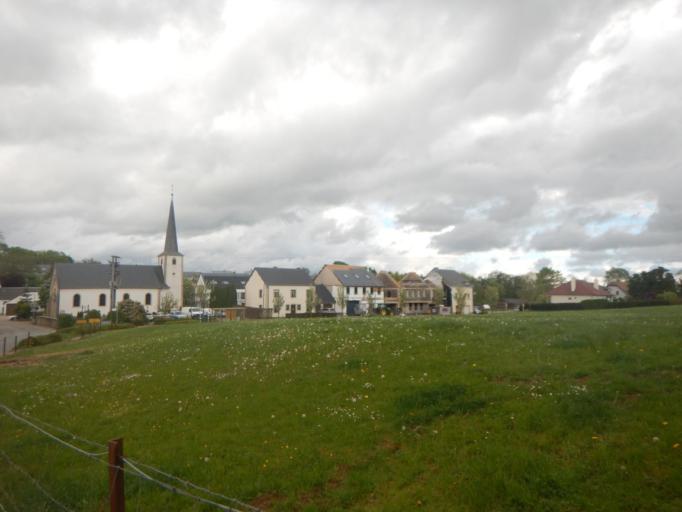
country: LU
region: Luxembourg
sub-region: Canton d'Esch-sur-Alzette
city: Mondercange
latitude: 49.5573
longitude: 5.9792
